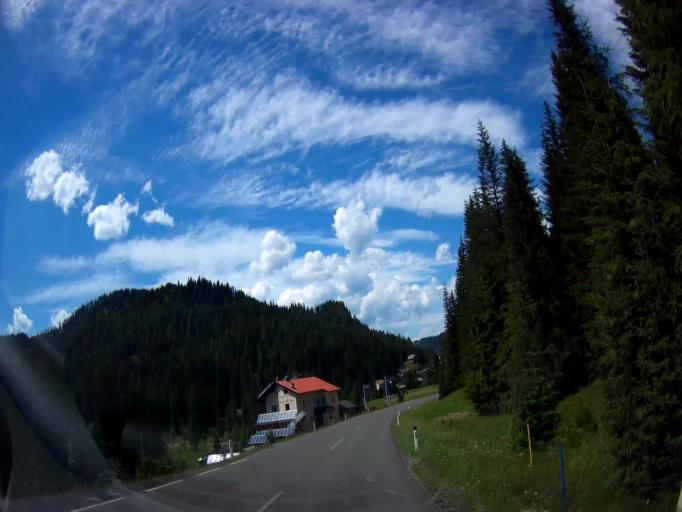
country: AT
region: Carinthia
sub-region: Politischer Bezirk Sankt Veit an der Glan
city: Glodnitz
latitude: 46.9490
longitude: 14.0252
